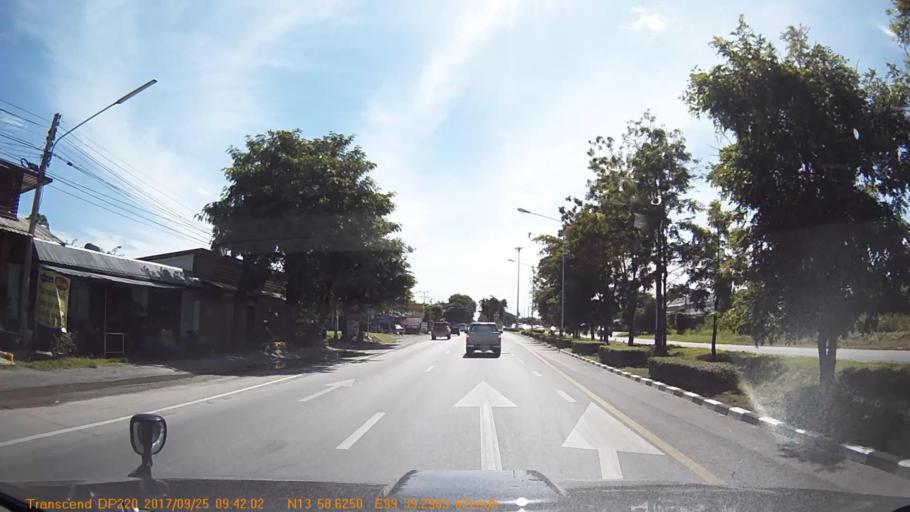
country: TH
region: Kanchanaburi
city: Tha Muang
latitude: 13.9770
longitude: 99.6552
